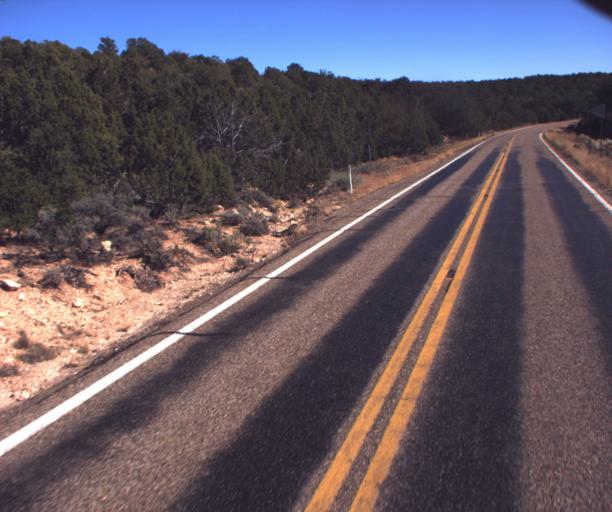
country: US
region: Arizona
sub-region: Coconino County
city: Fredonia
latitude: 36.7385
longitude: -112.1006
